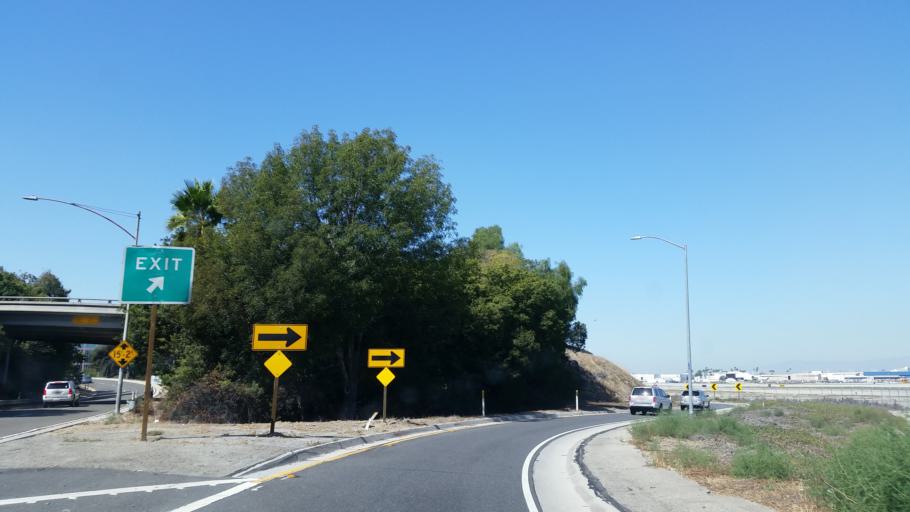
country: US
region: California
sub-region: Los Angeles County
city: Signal Hill
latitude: 33.8051
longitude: -118.1399
